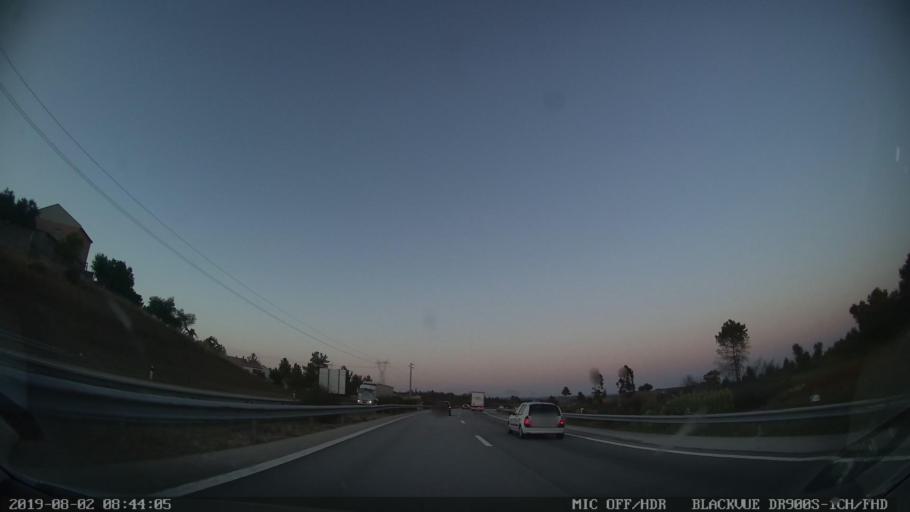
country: PT
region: Santarem
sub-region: Abrantes
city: Abrantes
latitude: 39.4923
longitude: -8.2066
